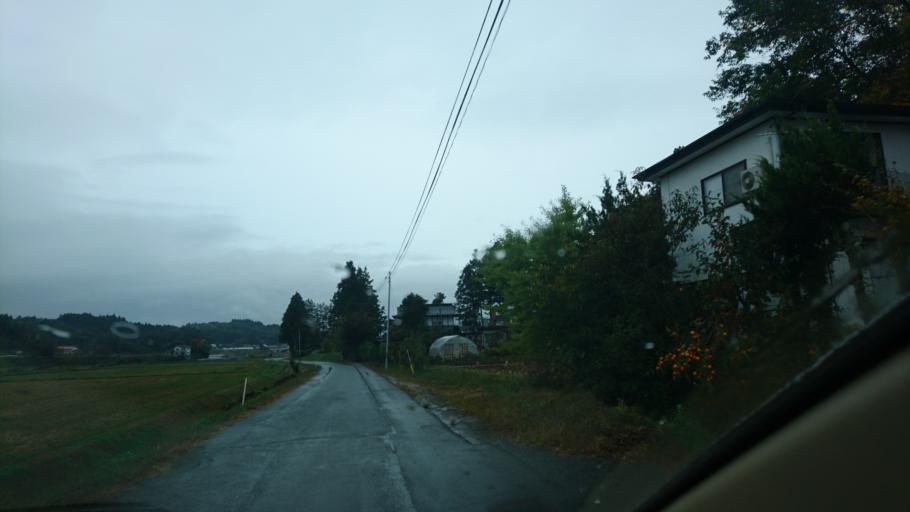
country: JP
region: Iwate
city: Ichinoseki
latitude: 38.9205
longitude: 141.1769
